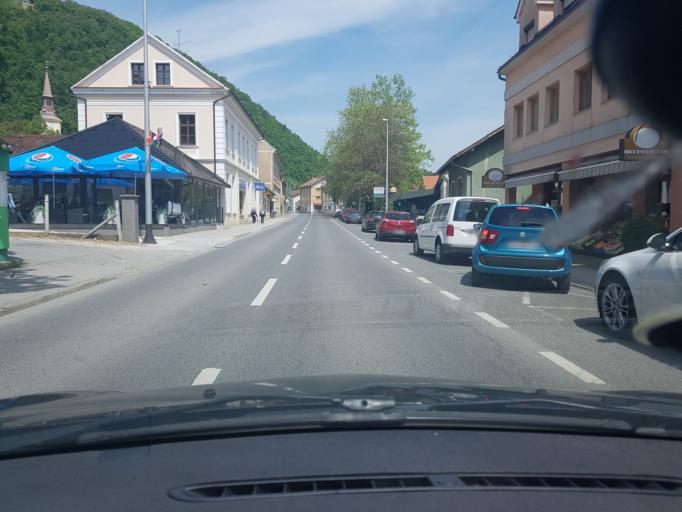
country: HR
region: Krapinsko-Zagorska
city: Pregrada
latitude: 46.1634
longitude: 15.7502
